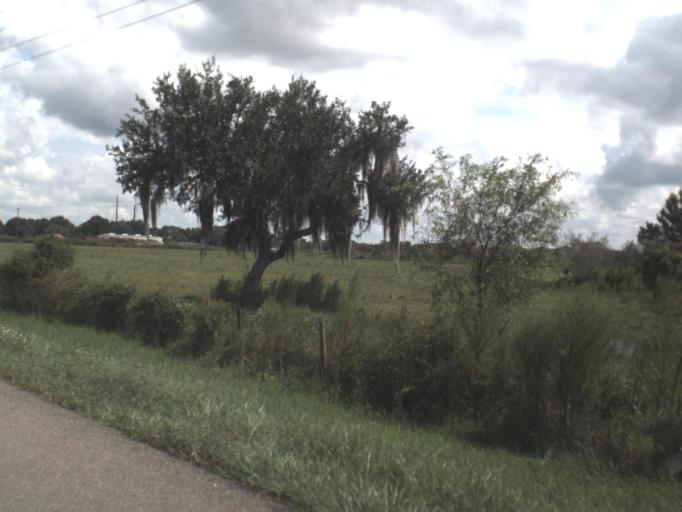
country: US
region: Florida
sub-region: Hardee County
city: Zolfo Springs
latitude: 27.4823
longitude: -81.9256
